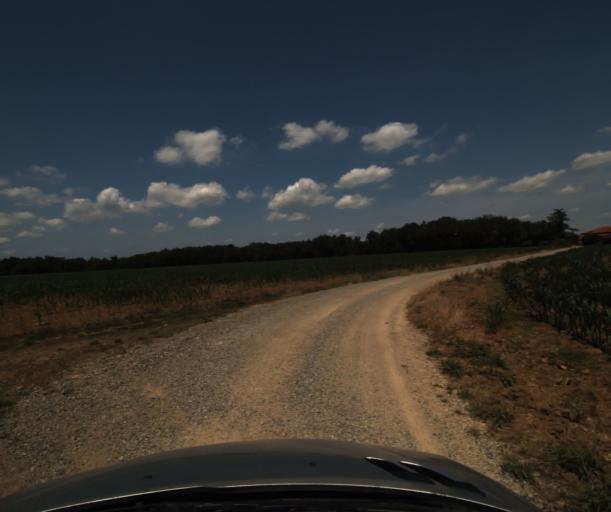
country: FR
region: Midi-Pyrenees
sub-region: Departement de la Haute-Garonne
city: Saint-Lys
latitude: 43.4812
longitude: 1.1966
